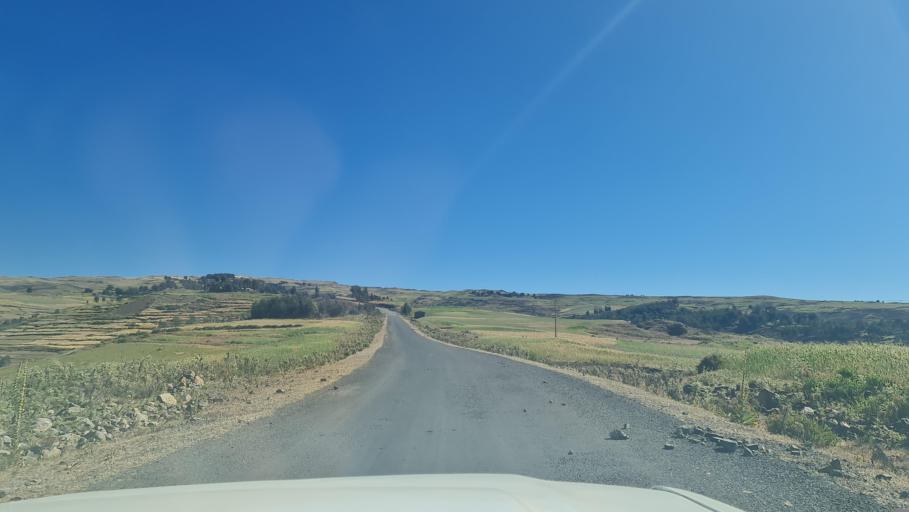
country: ET
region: Amhara
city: Debark'
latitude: 13.1138
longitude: 38.1504
